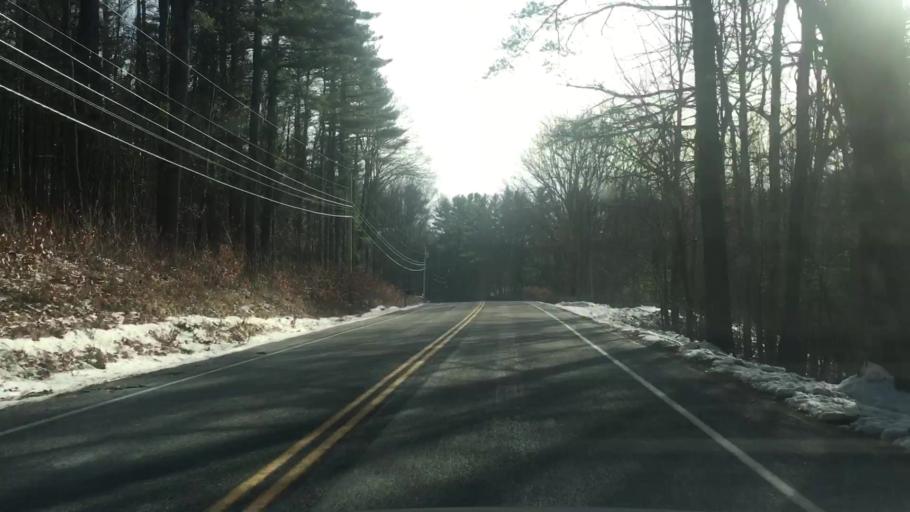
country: US
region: New Hampshire
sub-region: Merrimack County
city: Canterbury
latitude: 43.2983
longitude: -71.5636
